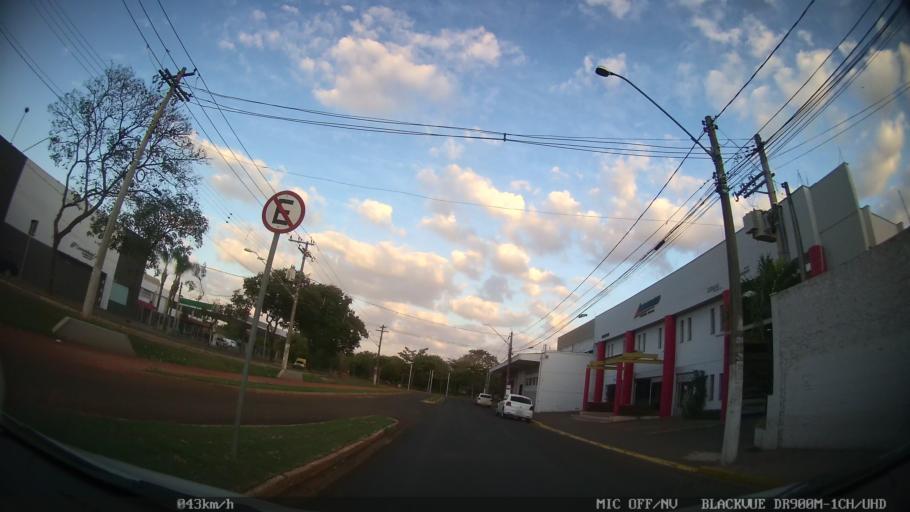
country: BR
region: Sao Paulo
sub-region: Ribeirao Preto
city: Ribeirao Preto
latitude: -21.1516
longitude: -47.7819
